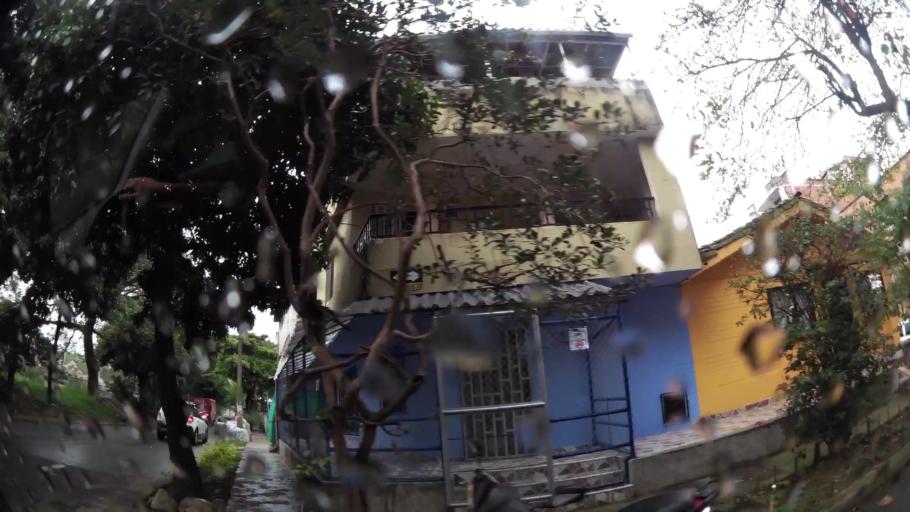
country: CO
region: Antioquia
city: Itagui
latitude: 6.1828
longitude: -75.5938
